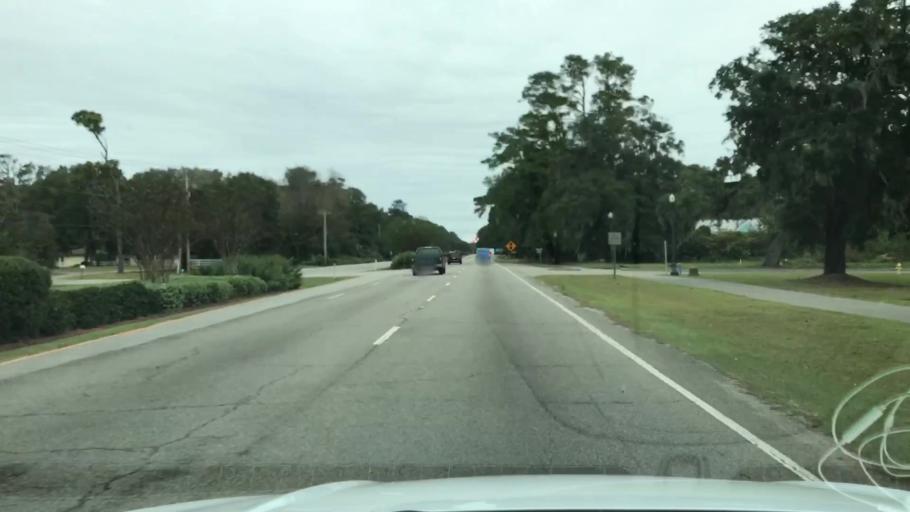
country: US
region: South Carolina
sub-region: Georgetown County
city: Murrells Inlet
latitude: 33.4883
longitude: -79.0925
